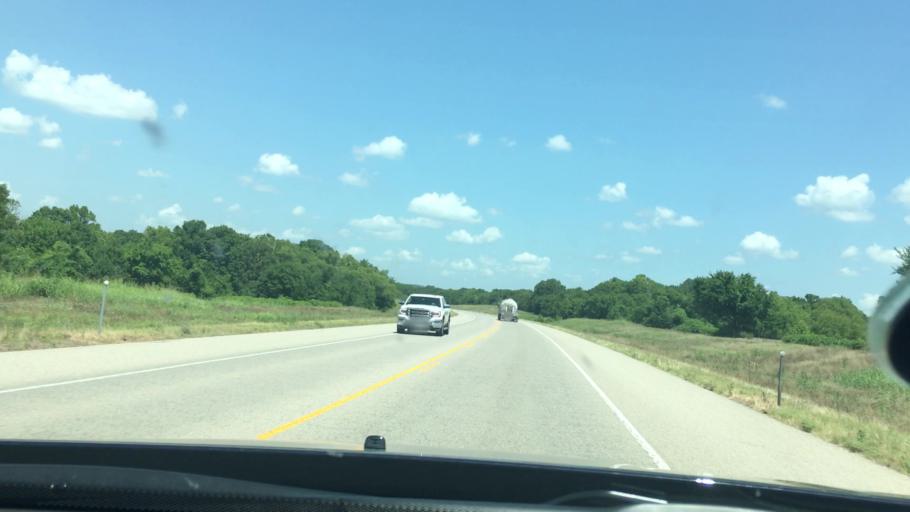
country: US
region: Oklahoma
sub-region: Pontotoc County
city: Ada
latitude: 34.6960
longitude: -96.5980
